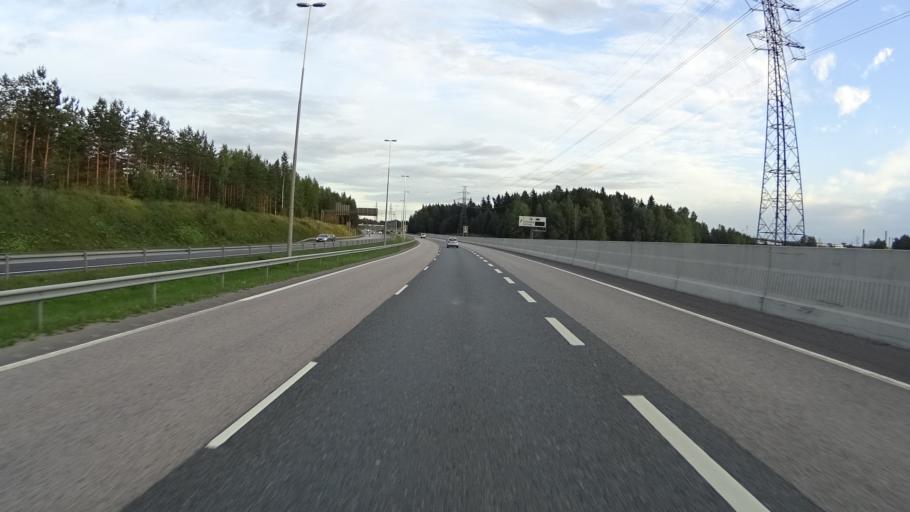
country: FI
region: Uusimaa
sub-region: Helsinki
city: Kilo
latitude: 60.3014
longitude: 24.8477
